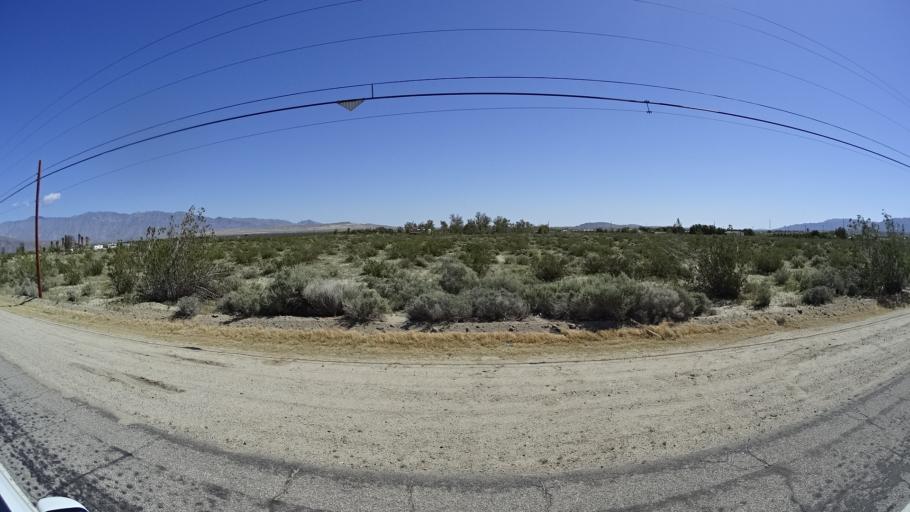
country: US
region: California
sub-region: San Diego County
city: Borrego Springs
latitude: 33.2236
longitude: -116.3476
